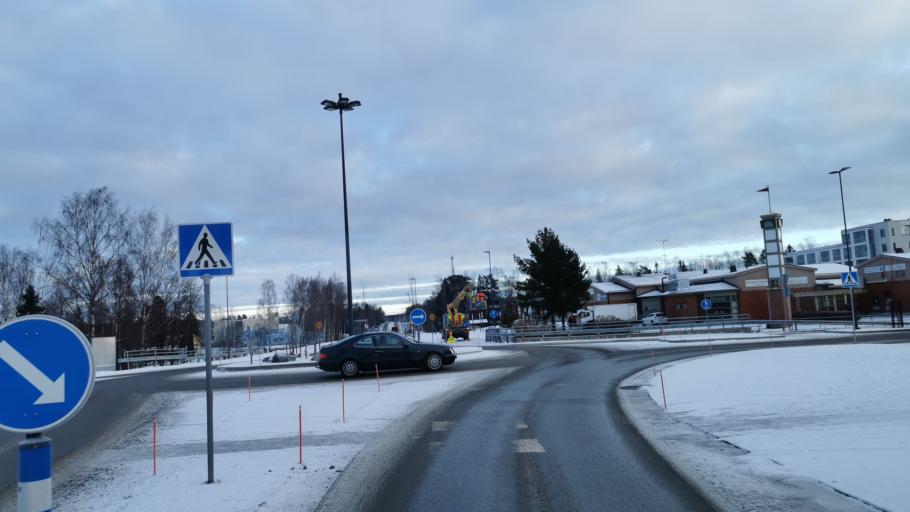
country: FI
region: Ostrobothnia
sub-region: Vaasa
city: Korsholm
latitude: 63.1126
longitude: 21.6765
